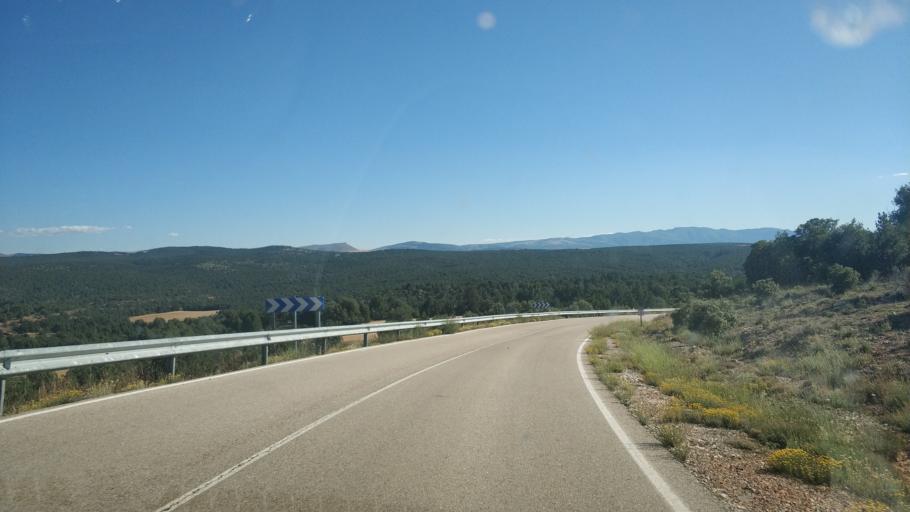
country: ES
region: Castille and Leon
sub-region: Provincia de Soria
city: Liceras
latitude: 41.4480
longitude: -3.2145
